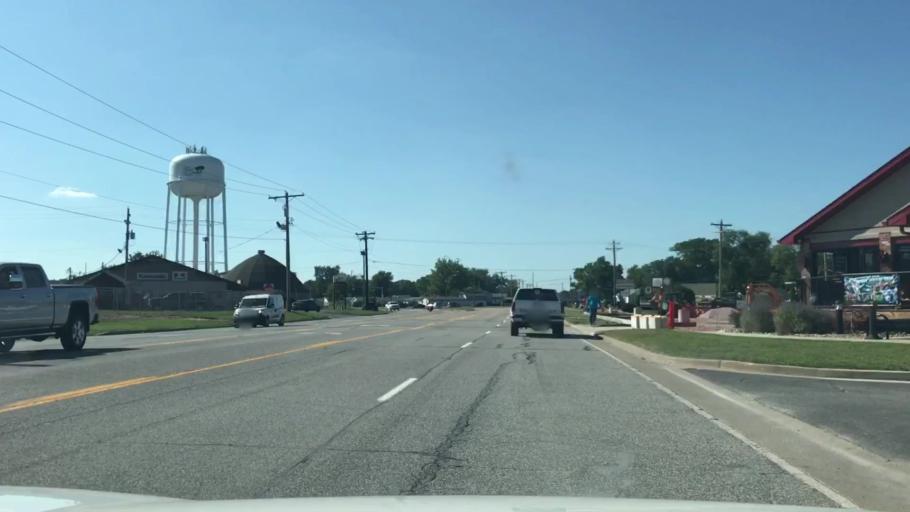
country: US
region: Illinois
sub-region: Madison County
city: Roxana
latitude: 38.8602
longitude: -90.0720
